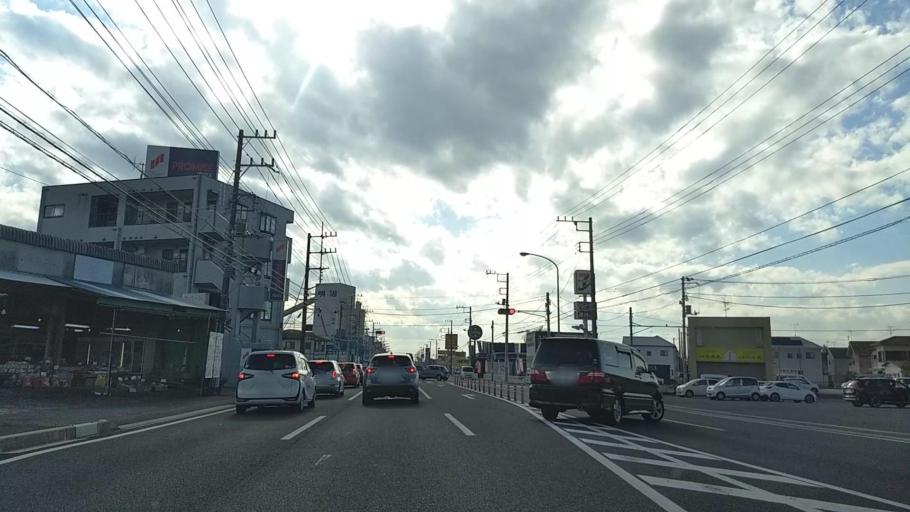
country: JP
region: Chiba
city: Togane
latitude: 35.5733
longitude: 140.3799
